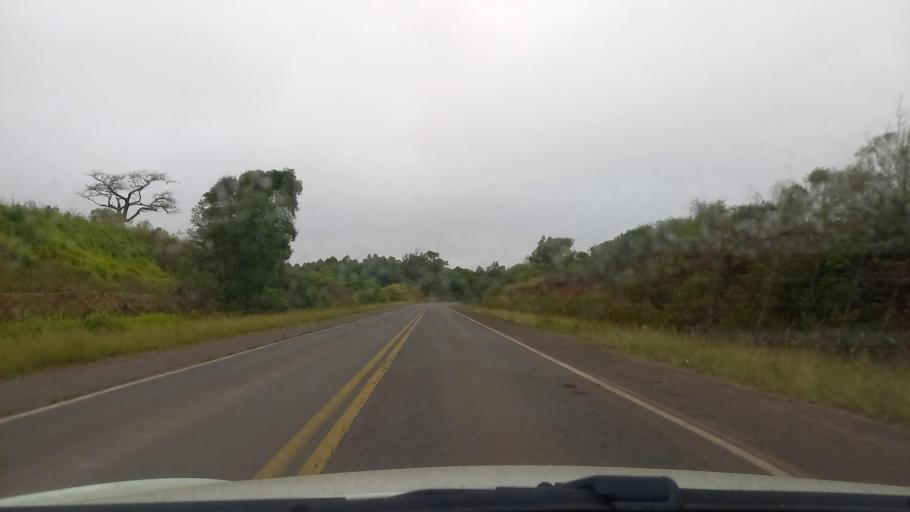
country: BR
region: Rio Grande do Sul
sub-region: Cacequi
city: Cacequi
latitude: -30.0976
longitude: -54.6299
